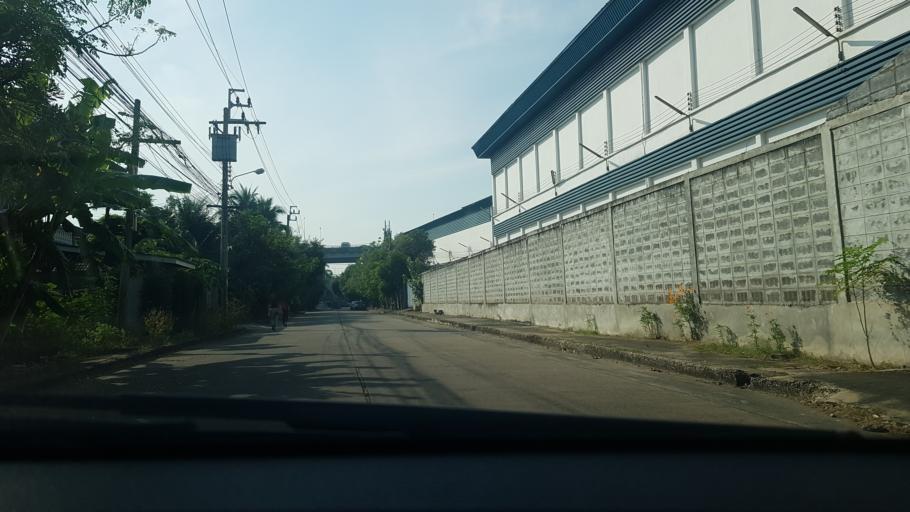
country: TH
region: Bangkok
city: Thawi Watthana
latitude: 13.7879
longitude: 100.3802
